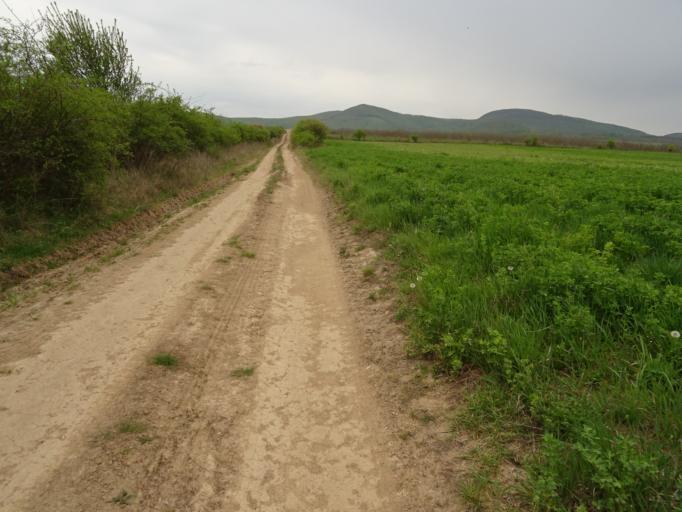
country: HU
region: Borsod-Abauj-Zemplen
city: Satoraljaujhely
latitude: 48.4313
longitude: 21.6239
